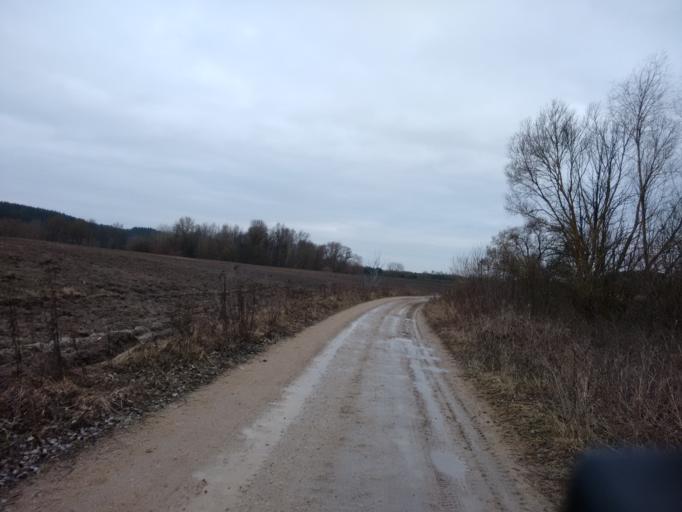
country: LT
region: Alytaus apskritis
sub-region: Alytus
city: Alytus
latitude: 54.2301
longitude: 23.9601
